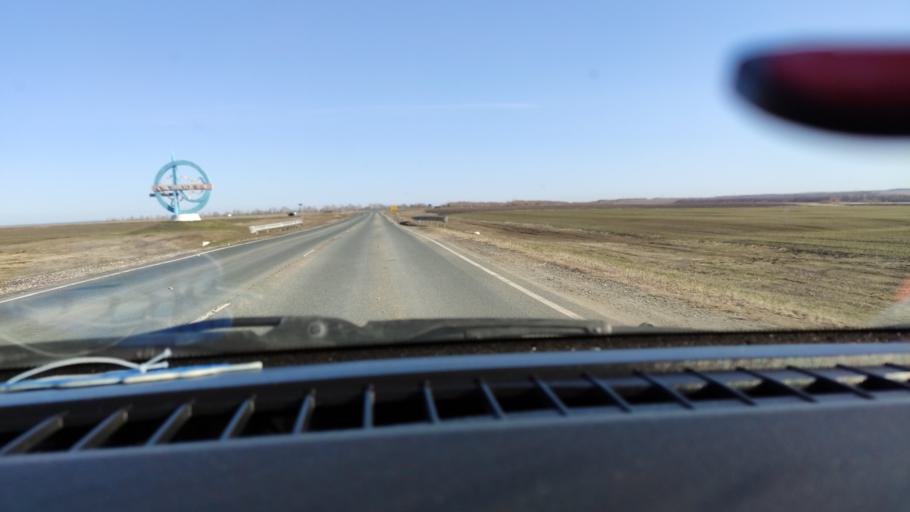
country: RU
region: Saratov
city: Dukhovnitskoye
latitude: 52.8034
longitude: 48.2298
